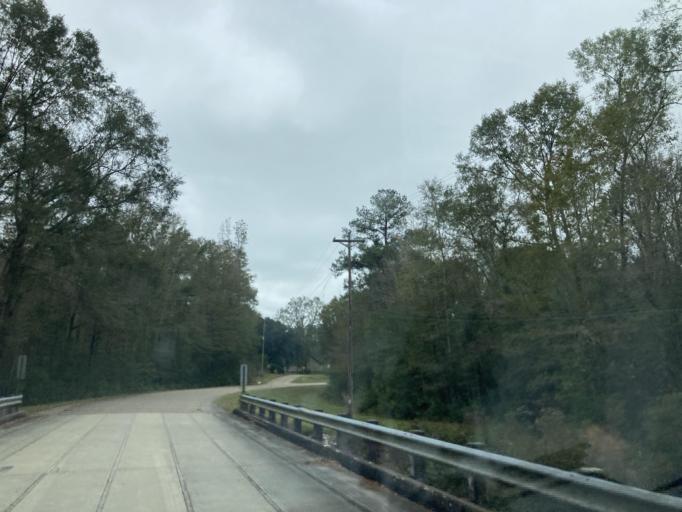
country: US
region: Mississippi
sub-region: Lamar County
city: West Hattiesburg
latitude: 31.2519
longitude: -89.4934
